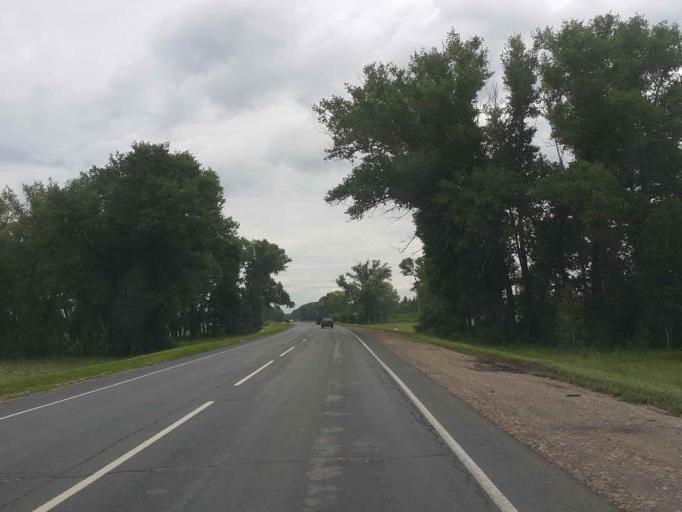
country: RU
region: Tambov
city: Zavoronezhskoye
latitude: 52.9516
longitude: 40.5826
